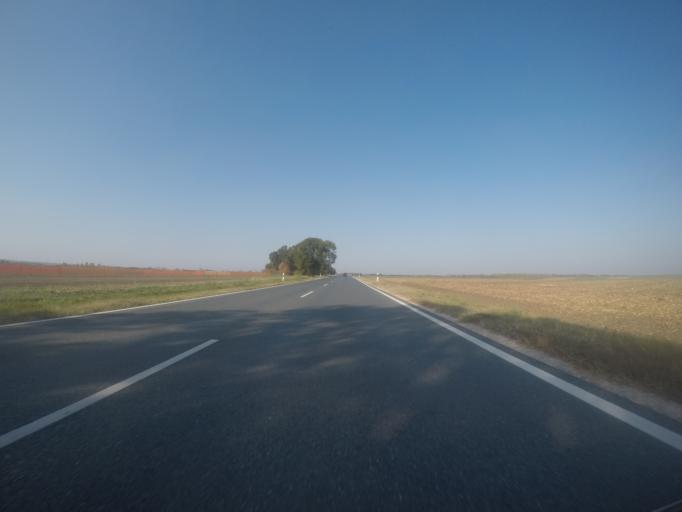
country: HU
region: Tolna
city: Madocsa
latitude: 46.7191
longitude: 18.8857
